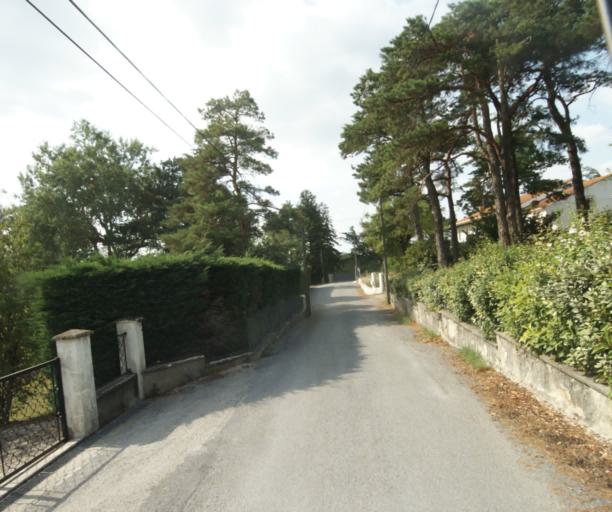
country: FR
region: Midi-Pyrenees
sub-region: Departement de la Haute-Garonne
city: Revel
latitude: 43.4433
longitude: 2.0295
